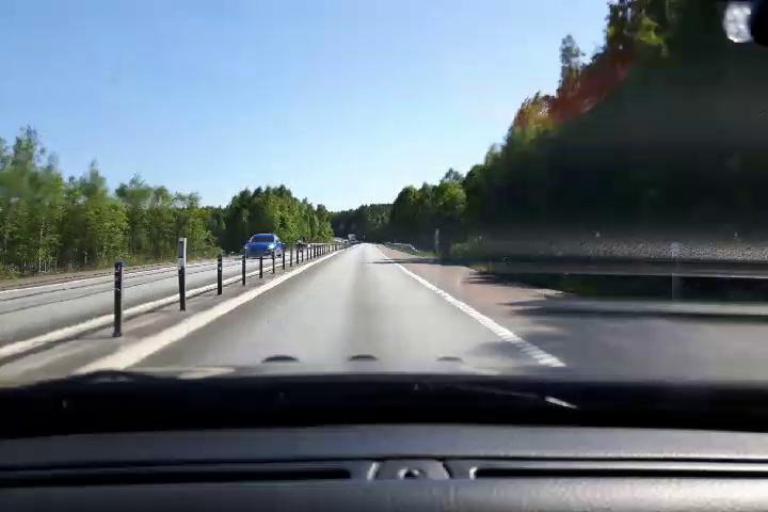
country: SE
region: Gaevleborg
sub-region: Soderhamns Kommun
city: Soderhamn
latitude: 61.2766
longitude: 17.0270
